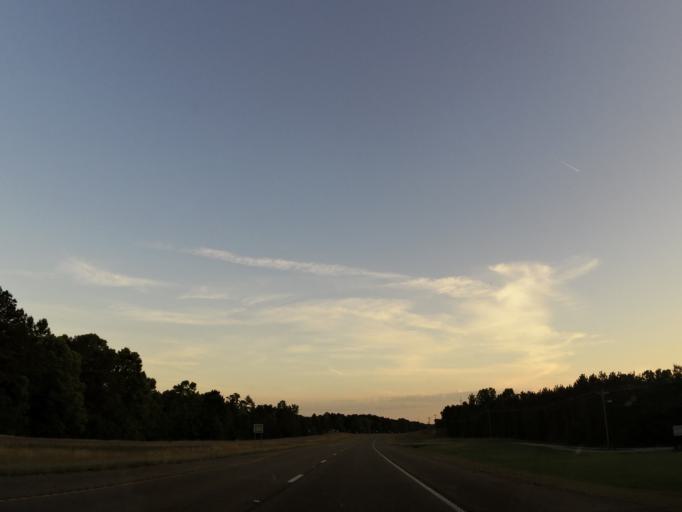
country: US
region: Mississippi
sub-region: Noxubee County
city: Macon
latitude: 33.0958
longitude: -88.5479
